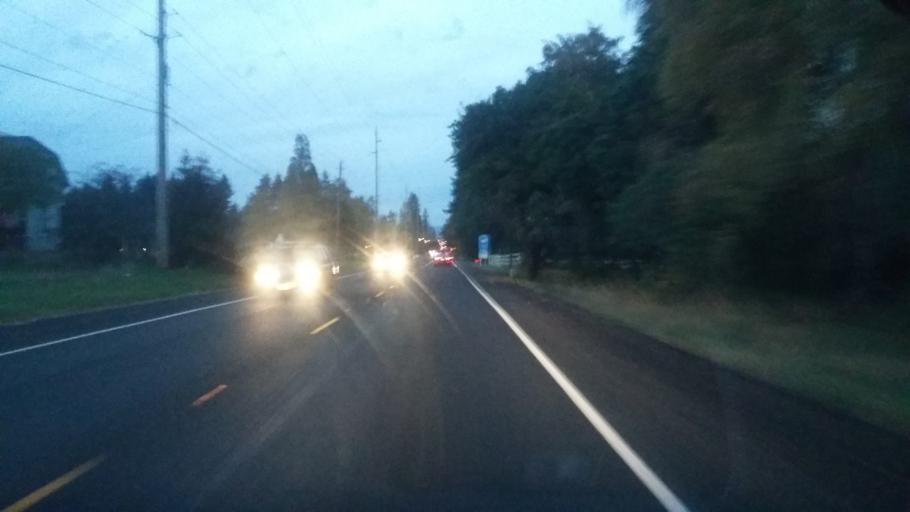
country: US
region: Washington
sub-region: Clark County
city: Barberton
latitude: 45.7160
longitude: -122.5994
